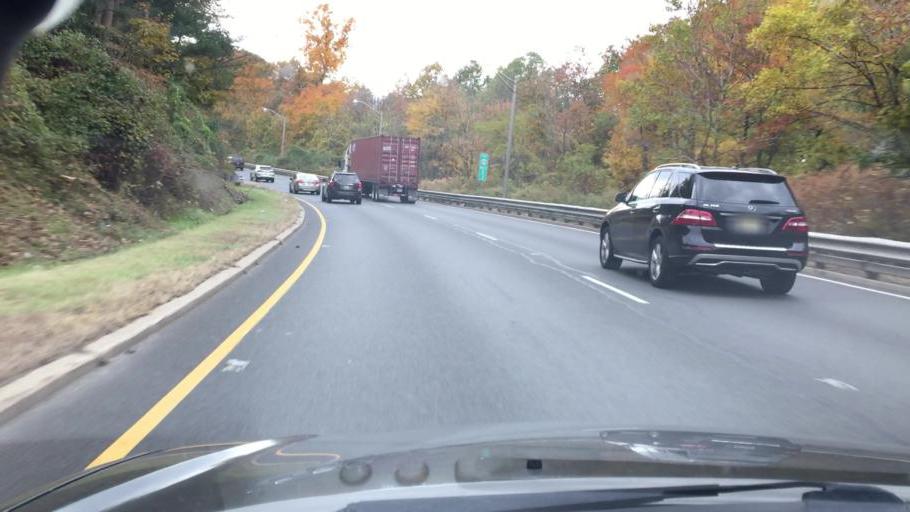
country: US
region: New Jersey
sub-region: Morris County
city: Morris Plains
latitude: 40.8131
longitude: -74.4480
